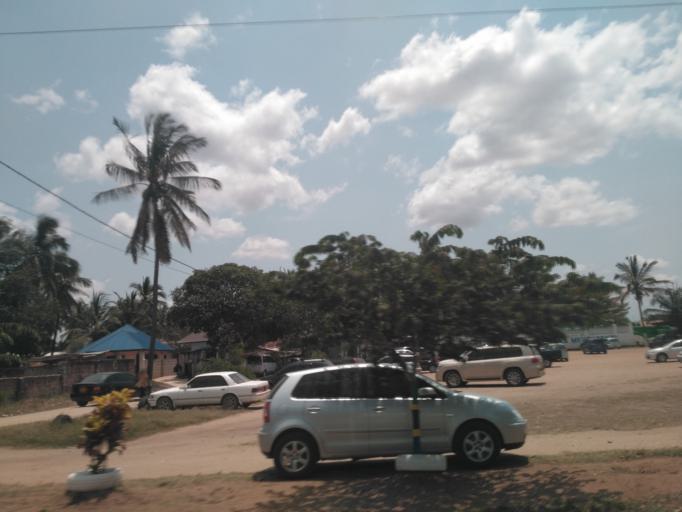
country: TZ
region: Dar es Salaam
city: Dar es Salaam
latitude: -6.8486
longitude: 39.3546
